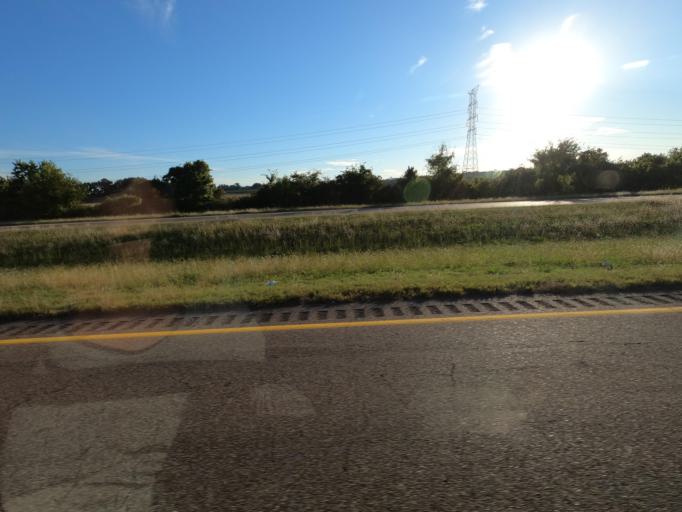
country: US
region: Tennessee
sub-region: Shelby County
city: Millington
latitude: 35.3251
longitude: -89.8833
